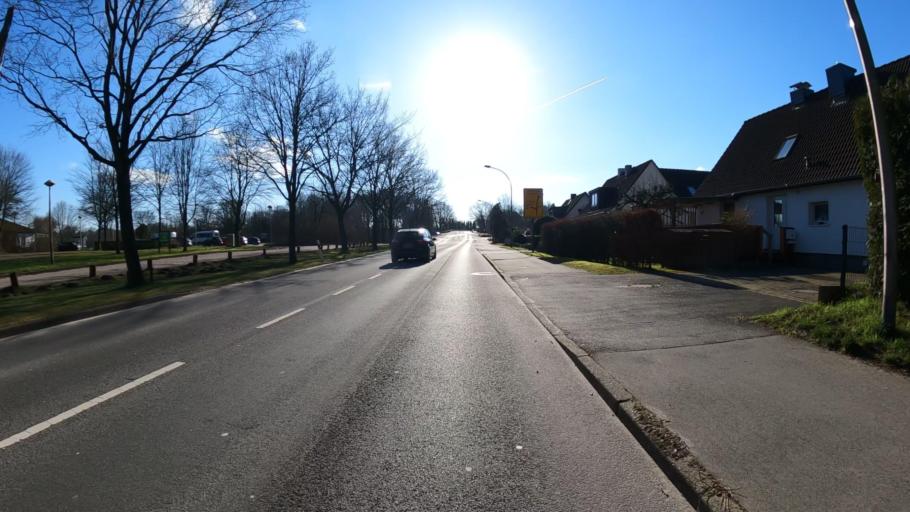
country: DE
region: Schleswig-Holstein
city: Rellingen
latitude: 53.6174
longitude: 9.7955
